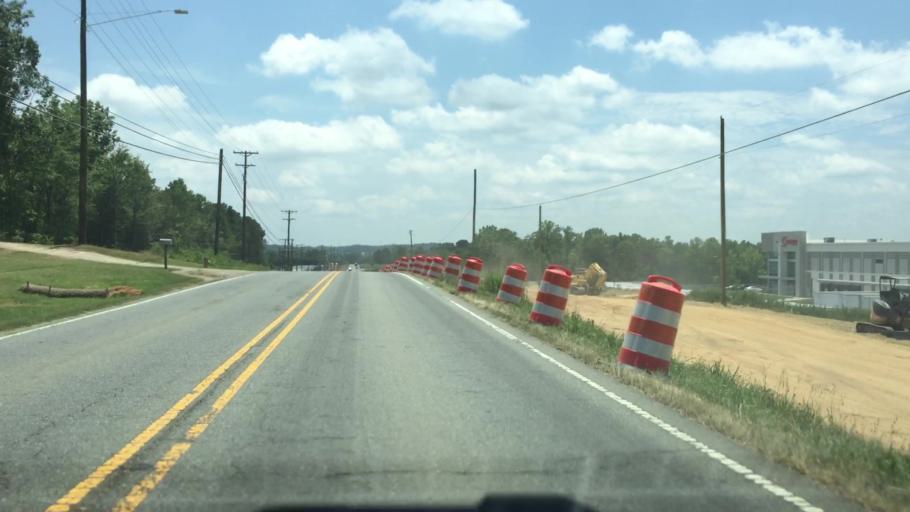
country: US
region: North Carolina
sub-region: Cabarrus County
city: Harrisburg
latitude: 35.3965
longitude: -80.7170
